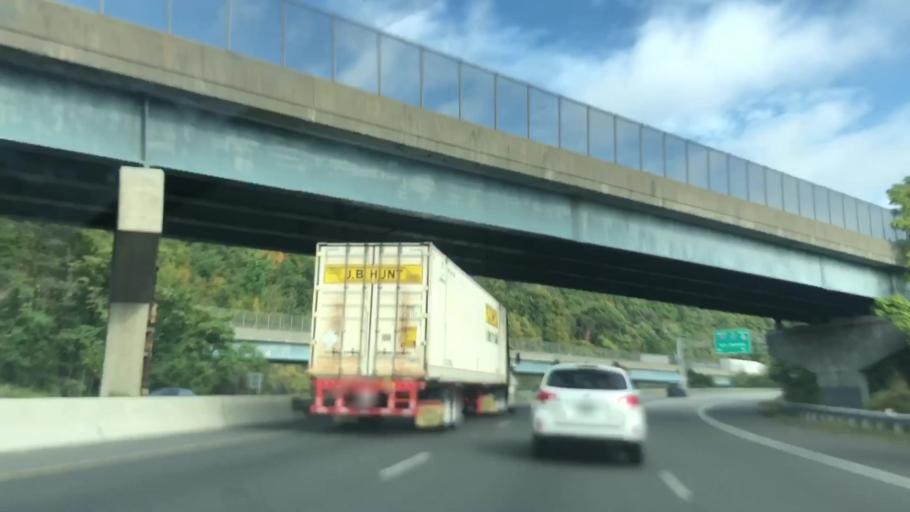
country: US
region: New York
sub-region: Rockland County
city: Suffern
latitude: 41.1036
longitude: -74.1675
